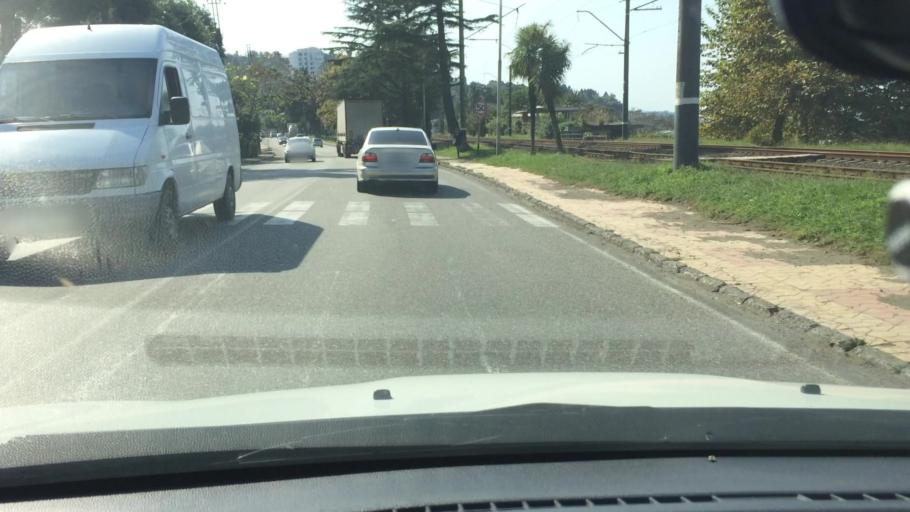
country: GE
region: Ajaria
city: Makhinjauri
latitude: 41.6808
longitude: 41.6983
